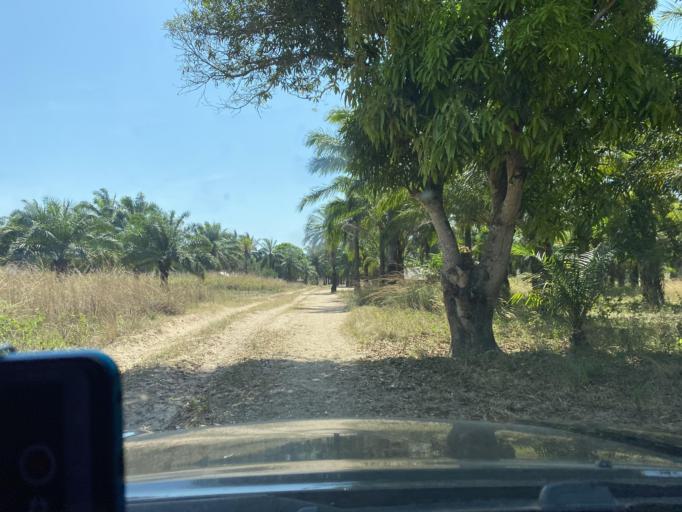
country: CD
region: Kasai-Oriental
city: Kabinda
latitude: -5.9088
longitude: 24.8487
